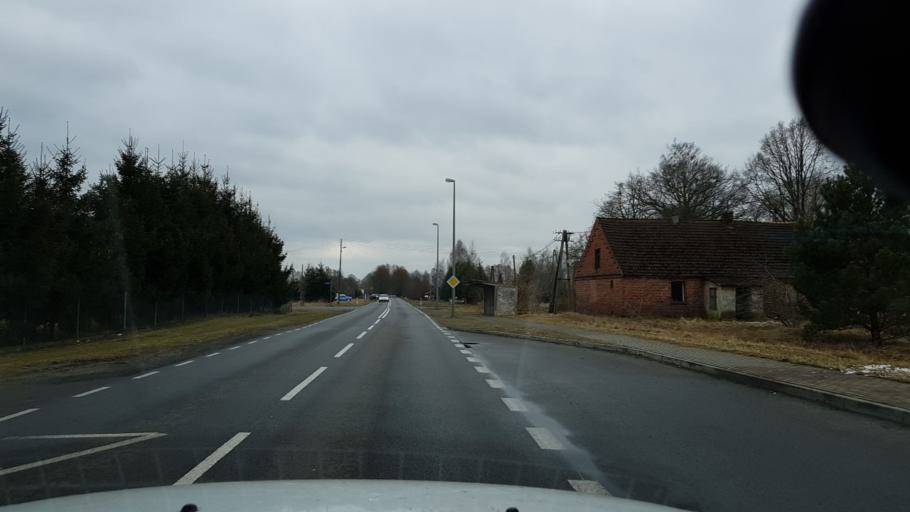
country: PL
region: West Pomeranian Voivodeship
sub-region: Powiat goleniowski
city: Goleniow
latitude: 53.5969
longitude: 14.7401
